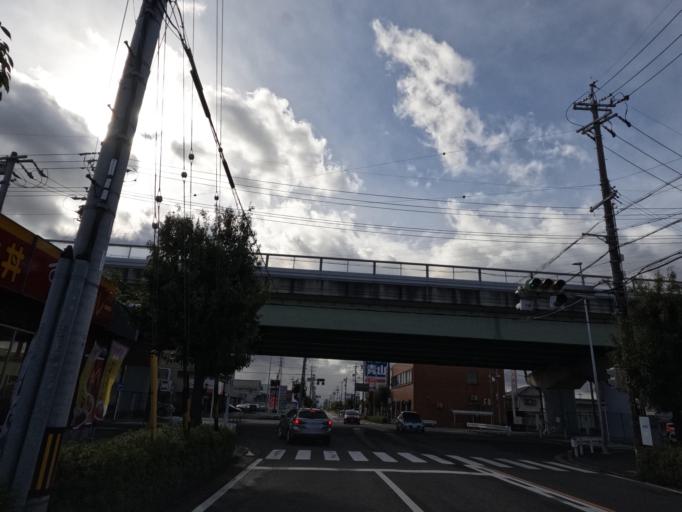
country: JP
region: Aichi
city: Chiryu
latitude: 35.0144
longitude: 137.0217
